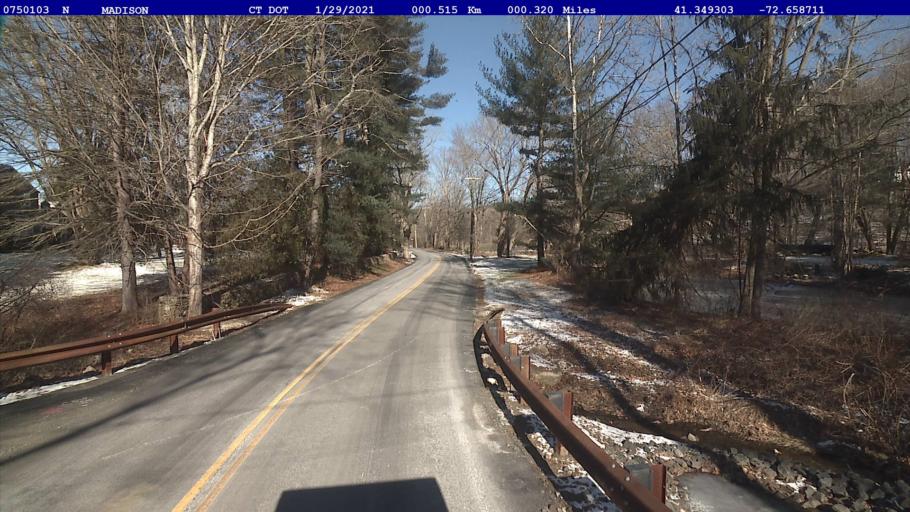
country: US
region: Connecticut
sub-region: New Haven County
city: Guilford
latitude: 41.3493
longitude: -72.6587
